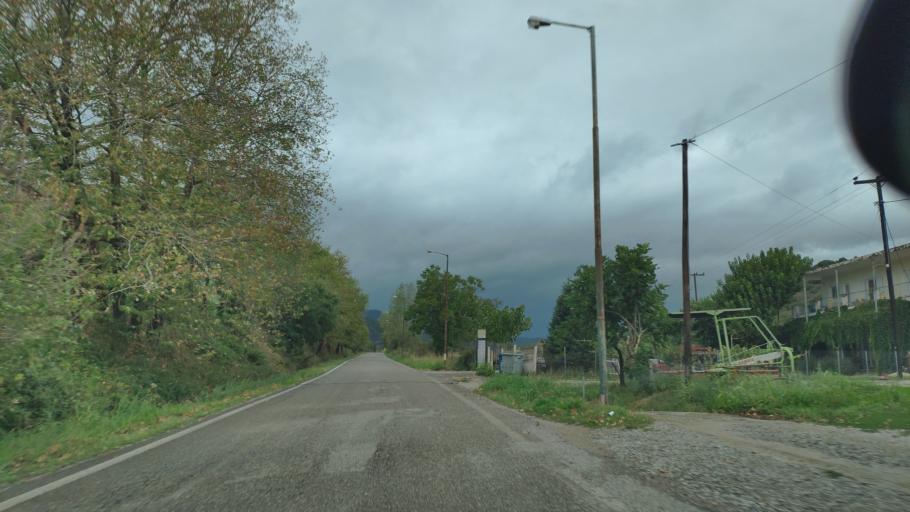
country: GR
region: West Greece
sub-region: Nomos Aitolias kai Akarnanias
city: Krikellos
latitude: 38.9747
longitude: 21.3297
